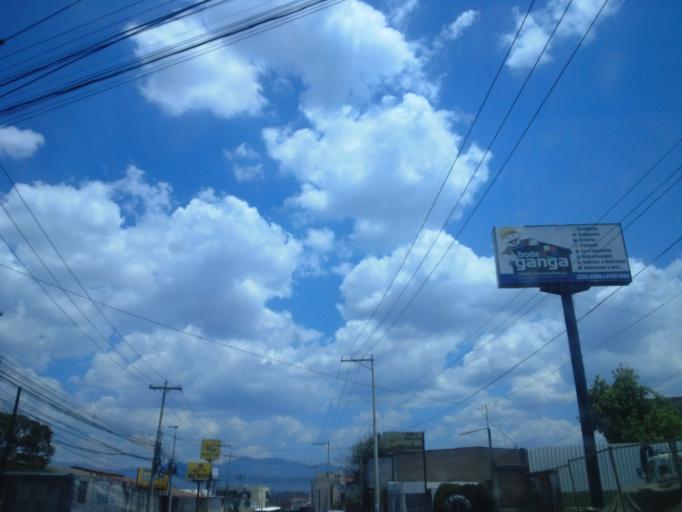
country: HN
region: Francisco Morazan
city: Tegucigalpa
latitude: 14.0601
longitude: -87.2268
